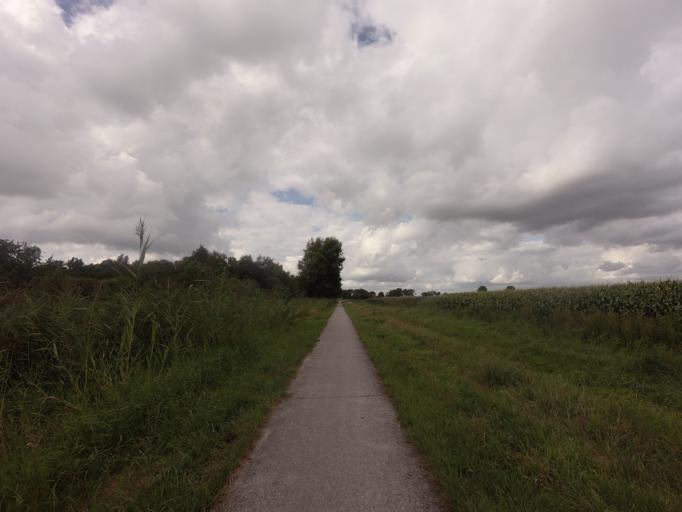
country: NL
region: Overijssel
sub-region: Gemeente Steenwijkerland
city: Giethoorn
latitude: 52.7348
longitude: 6.0517
